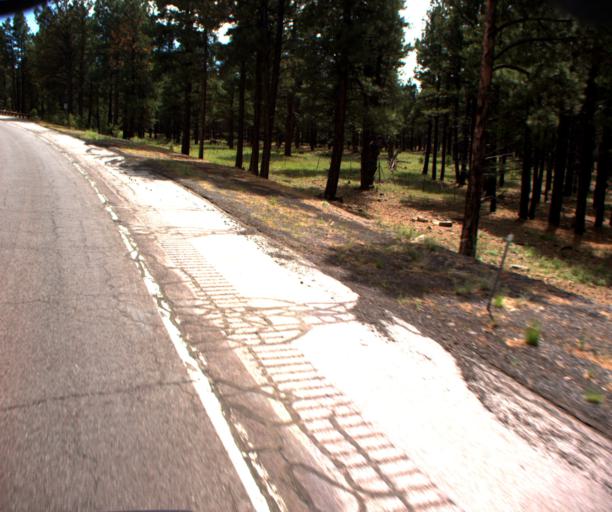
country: US
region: Arizona
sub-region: Coconino County
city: Parks
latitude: 35.4332
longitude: -111.7631
